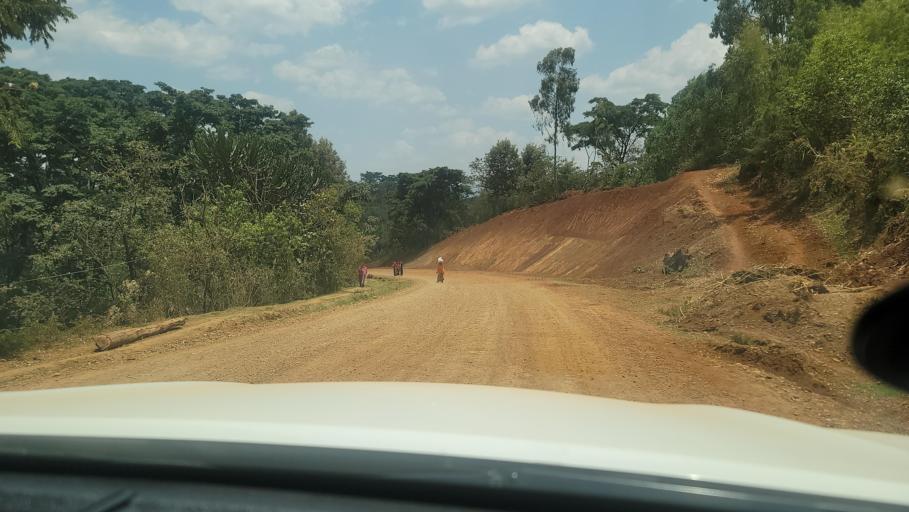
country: ET
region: Oromiya
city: Agaro
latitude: 7.8040
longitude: 36.4650
